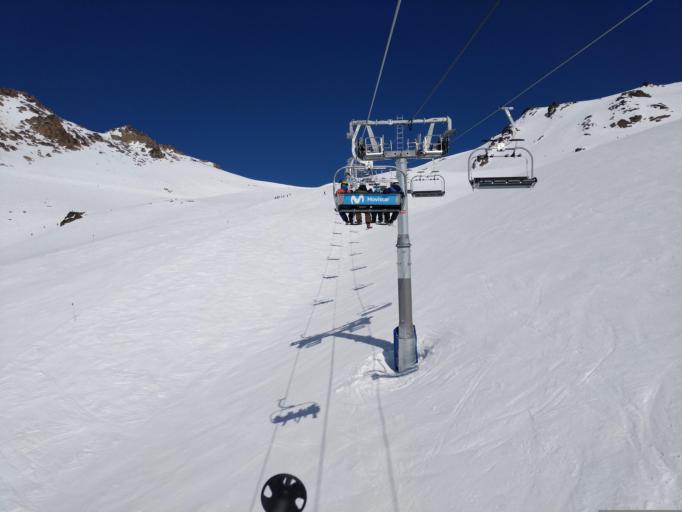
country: AR
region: Rio Negro
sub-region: Departamento de Bariloche
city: San Carlos de Bariloche
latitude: -41.1700
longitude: -71.4774
